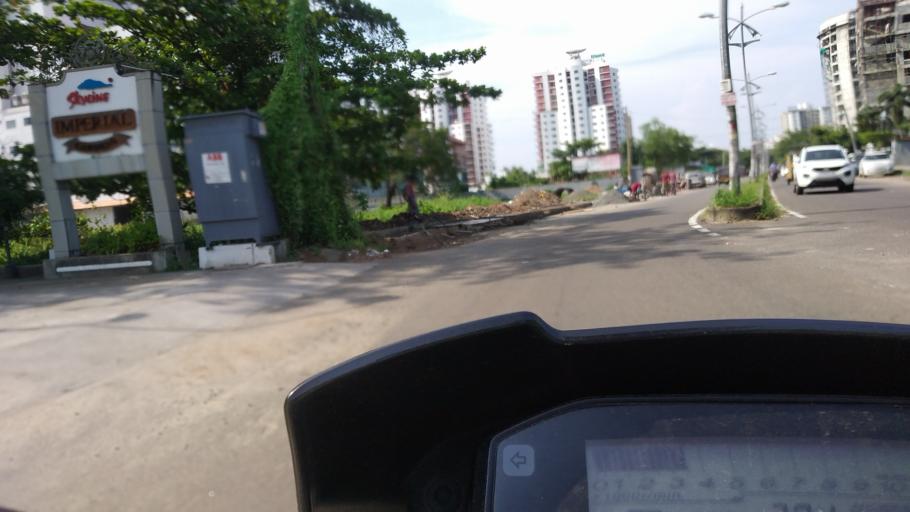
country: IN
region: Kerala
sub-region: Ernakulam
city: Cochin
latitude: 9.9878
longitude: 76.3020
